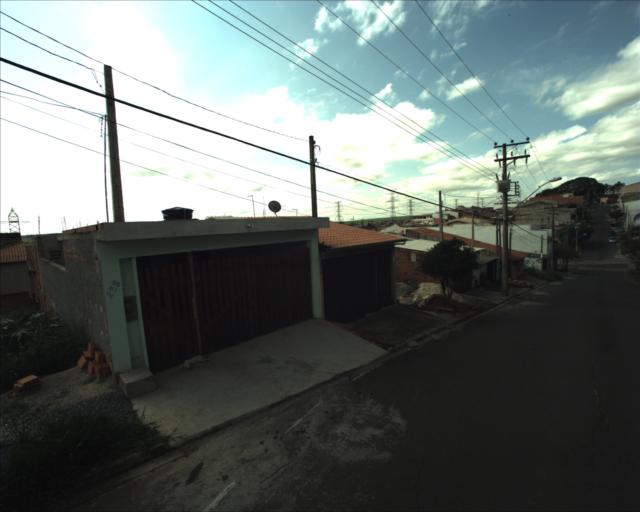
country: BR
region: Sao Paulo
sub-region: Sorocaba
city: Sorocaba
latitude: -23.3990
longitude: -47.3818
